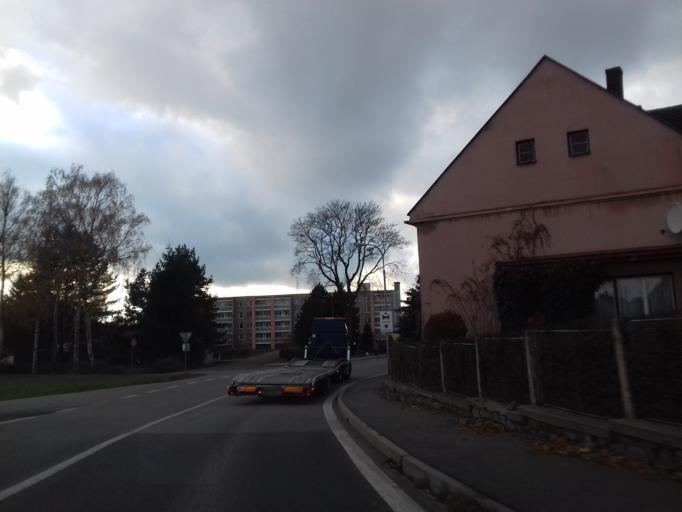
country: CZ
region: Pardubicky
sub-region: Okres Svitavy
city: Policka
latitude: 49.7187
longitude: 16.2843
